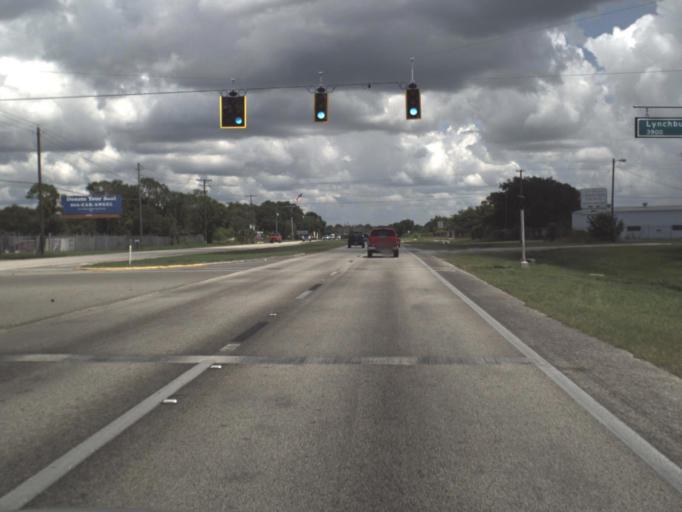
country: US
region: Florida
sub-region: Polk County
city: Inwood
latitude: 28.0675
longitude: -81.7517
